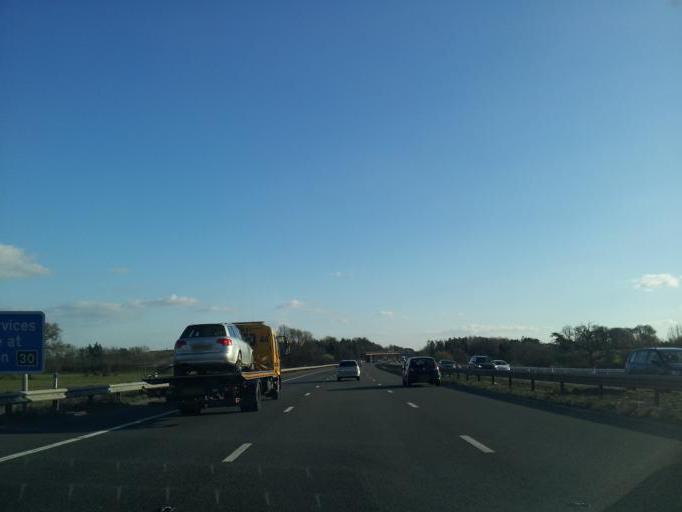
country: GB
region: England
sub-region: Devon
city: Heavitree
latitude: 50.7553
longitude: -3.4562
